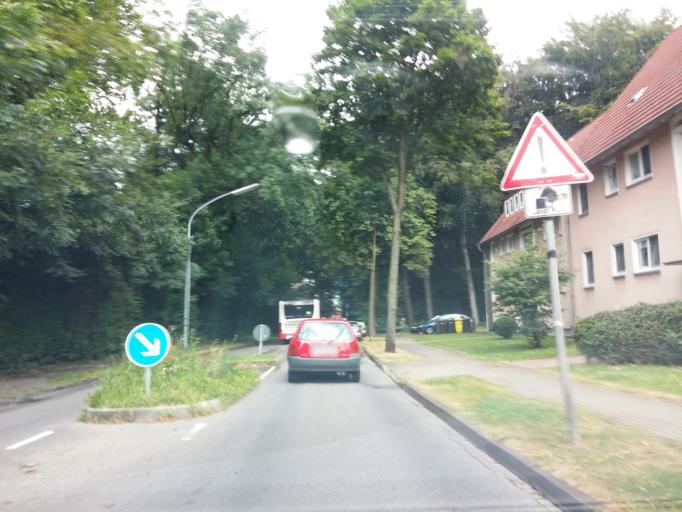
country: DE
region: North Rhine-Westphalia
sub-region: Regierungsbezirk Munster
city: Gladbeck
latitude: 51.5922
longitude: 7.0076
